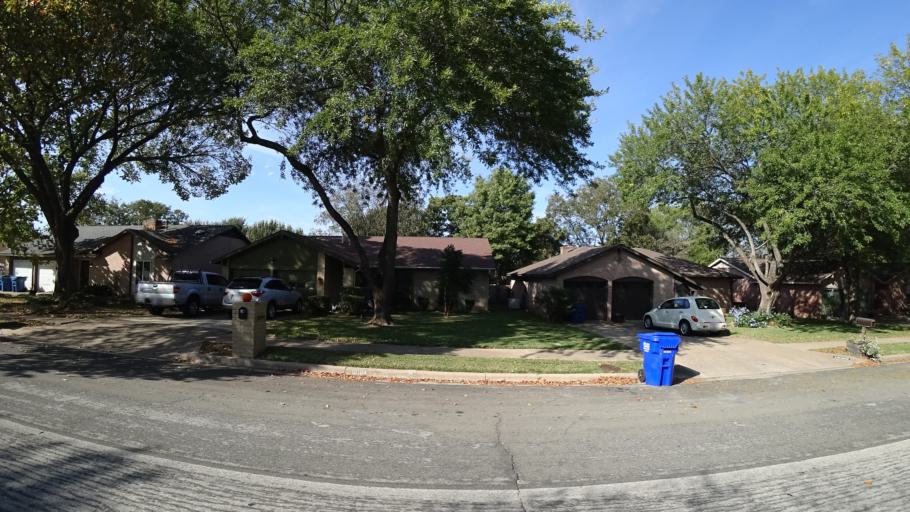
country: US
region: Texas
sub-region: Williamson County
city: Anderson Mill
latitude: 30.4495
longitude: -97.7992
